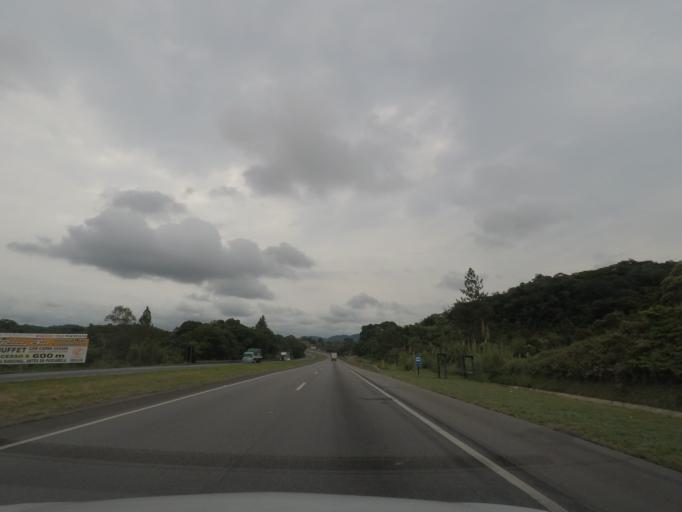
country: BR
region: Sao Paulo
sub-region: Juquia
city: Juquia
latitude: -24.3306
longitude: -47.6140
